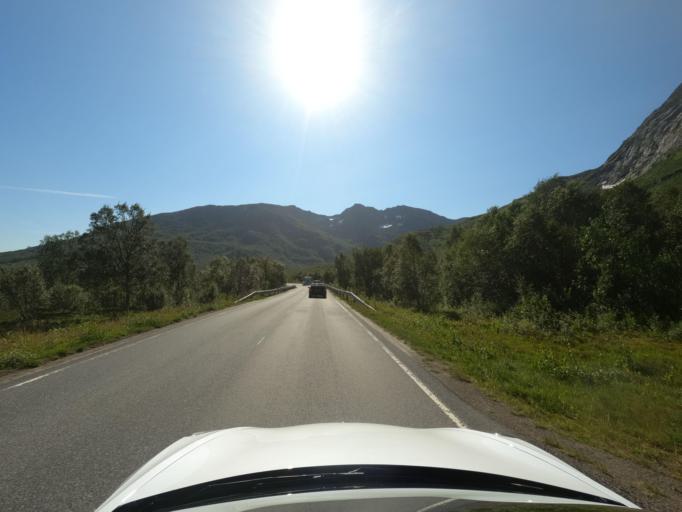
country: NO
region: Nordland
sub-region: Lodingen
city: Lodingen
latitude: 68.5315
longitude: 15.7275
